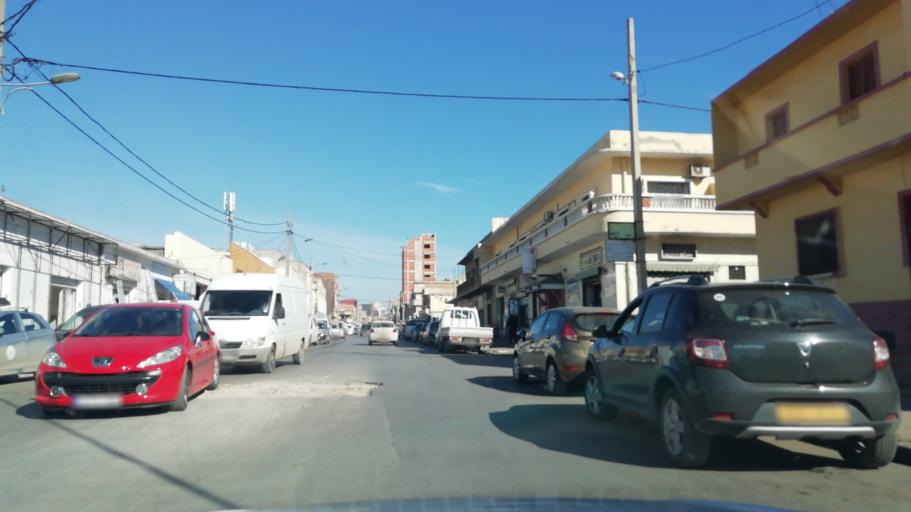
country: DZ
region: Oran
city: Oran
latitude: 35.6904
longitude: -0.6245
